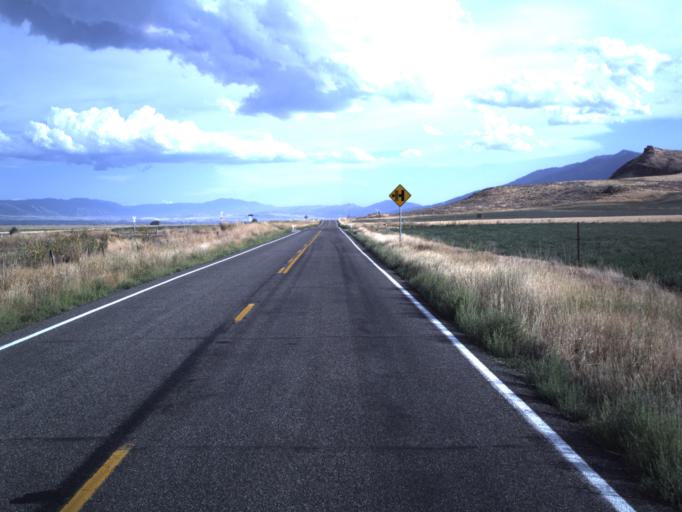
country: US
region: Utah
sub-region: Cache County
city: Benson
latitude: 41.8167
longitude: -111.9971
